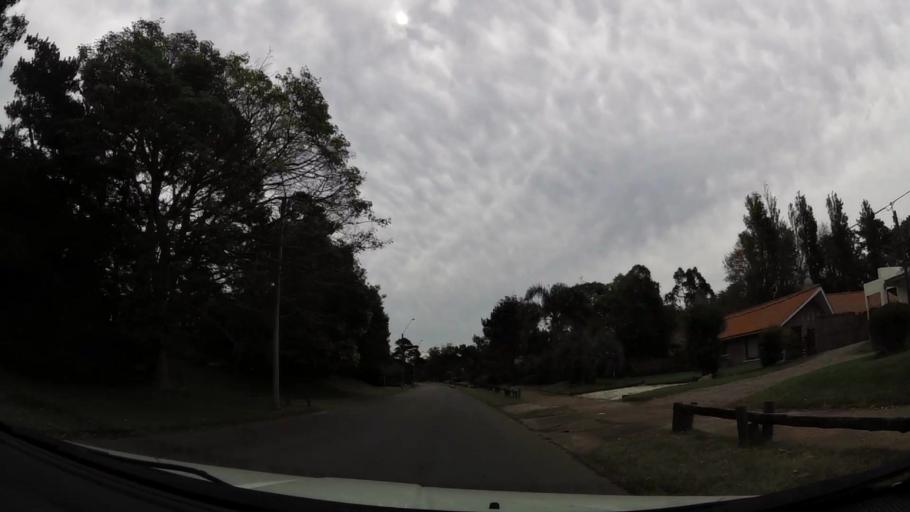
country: UY
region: Maldonado
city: Maldonado
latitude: -34.9072
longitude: -54.9965
